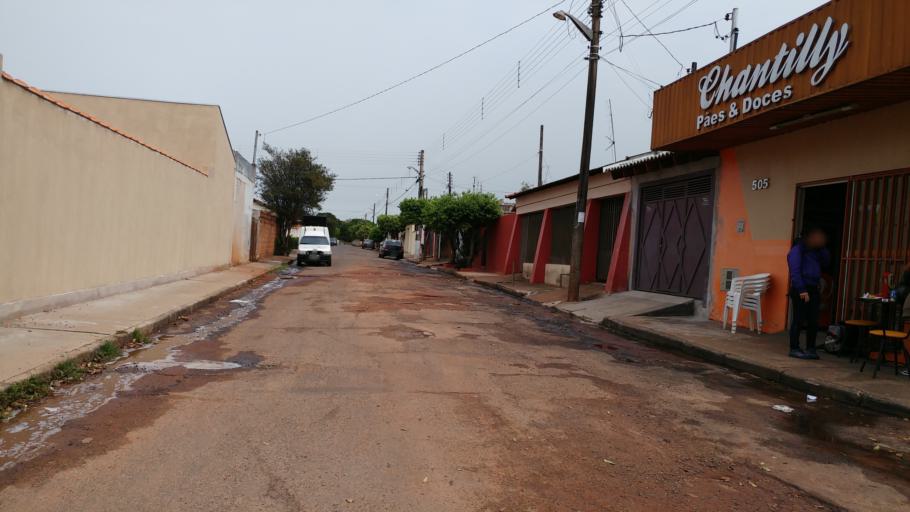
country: BR
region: Sao Paulo
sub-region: Paraguacu Paulista
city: Paraguacu Paulista
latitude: -22.4311
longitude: -50.5809
